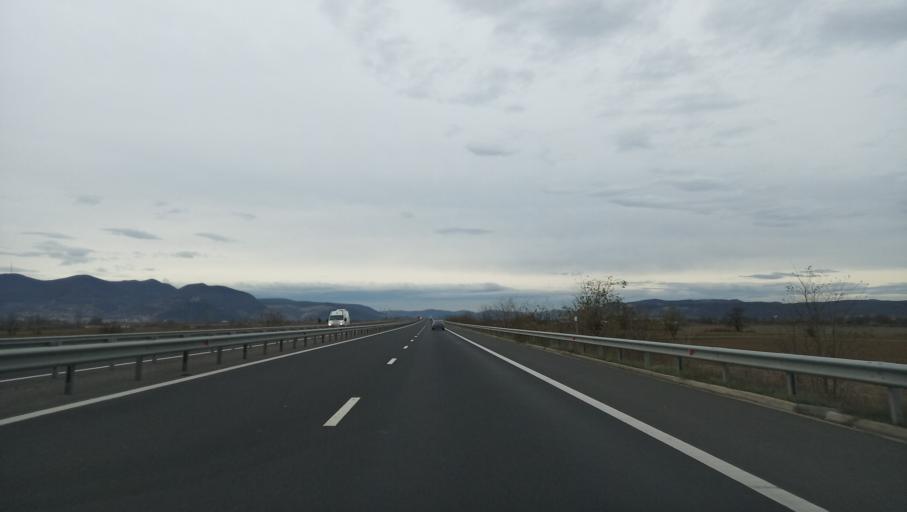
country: RO
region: Hunedoara
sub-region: Comuna Harau
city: Harau
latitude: 45.8900
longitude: 22.9649
